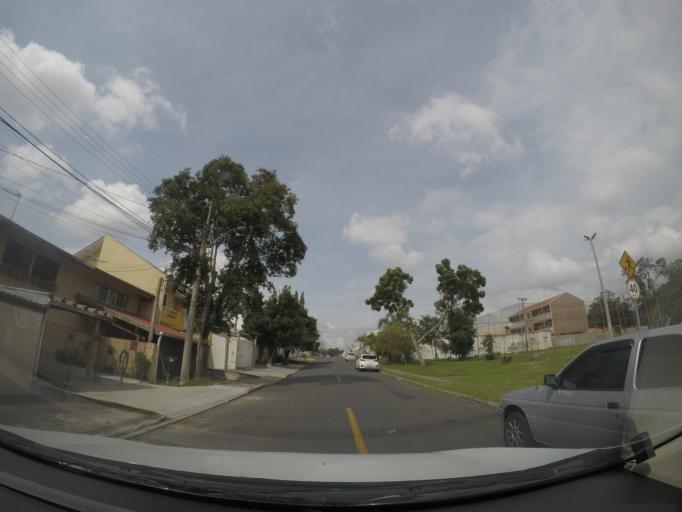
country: BR
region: Parana
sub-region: Curitiba
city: Curitiba
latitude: -25.4873
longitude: -49.2770
